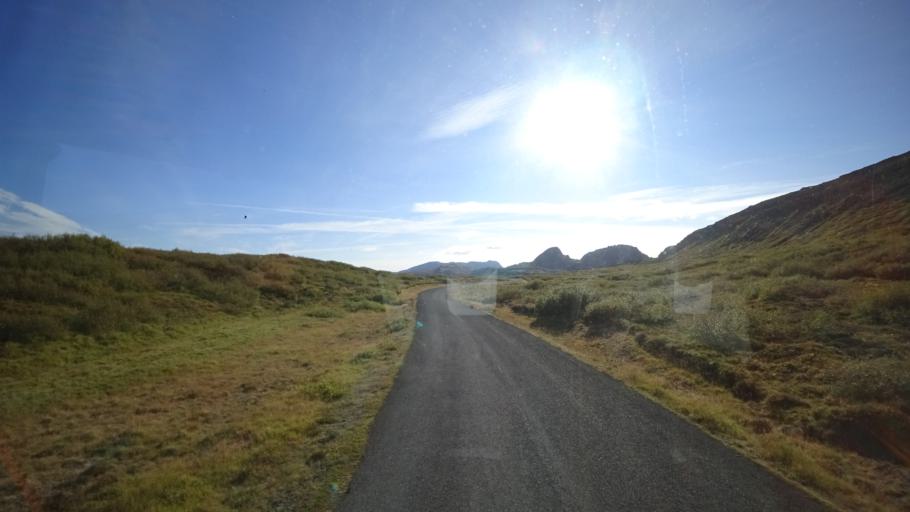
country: IS
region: South
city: Hveragerdi
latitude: 64.1611
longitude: -21.2467
